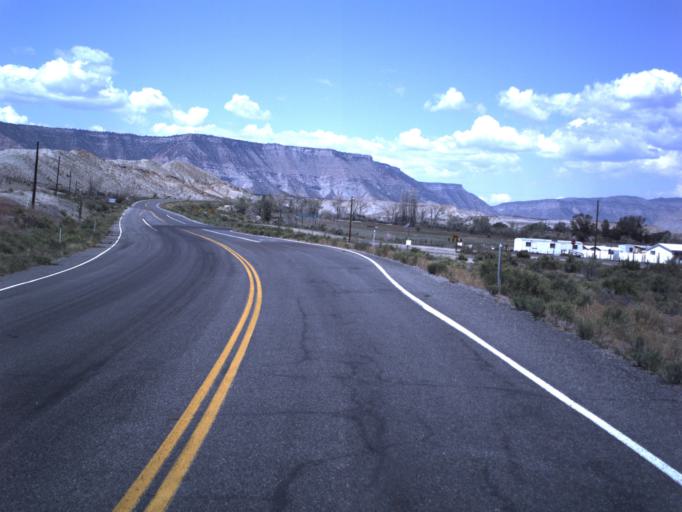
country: US
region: Utah
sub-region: Emery County
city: Orangeville
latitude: 39.2124
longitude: -111.0515
